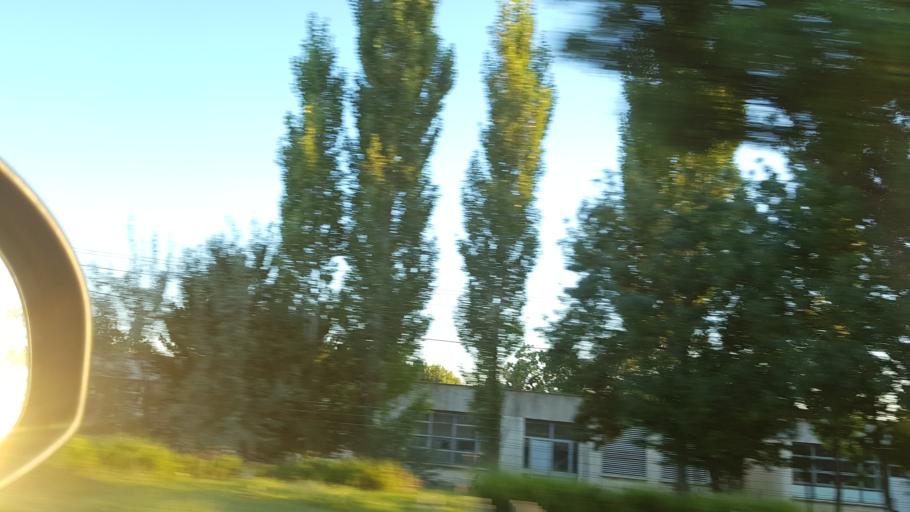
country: TR
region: Ankara
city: Etimesgut
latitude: 39.9626
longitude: 32.6619
